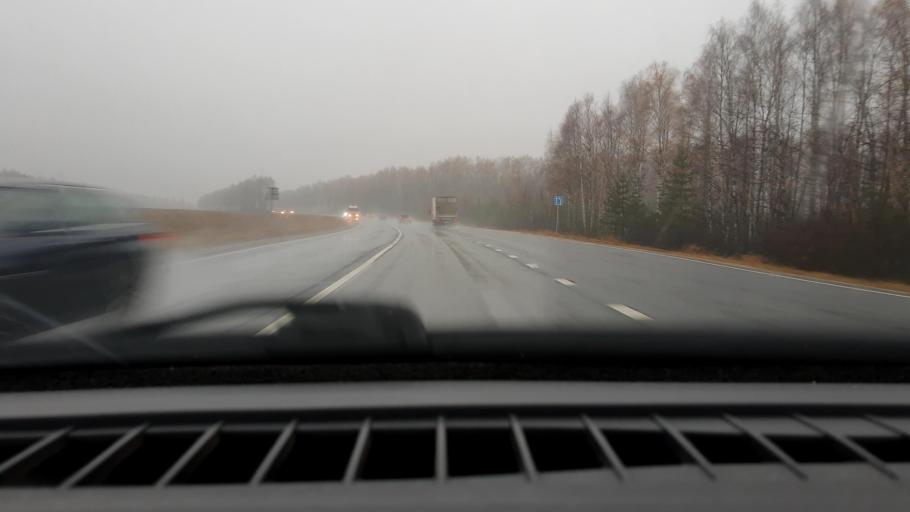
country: RU
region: Nizjnij Novgorod
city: Linda
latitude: 56.5797
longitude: 44.0232
